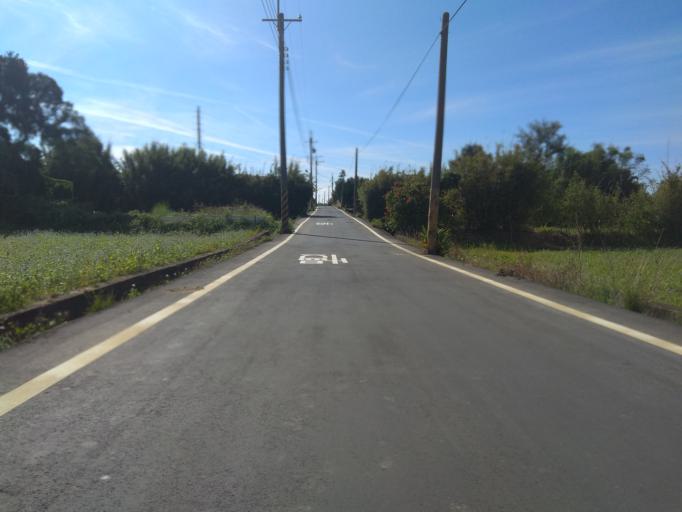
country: TW
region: Taiwan
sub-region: Hsinchu
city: Zhubei
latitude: 24.9936
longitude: 121.0412
